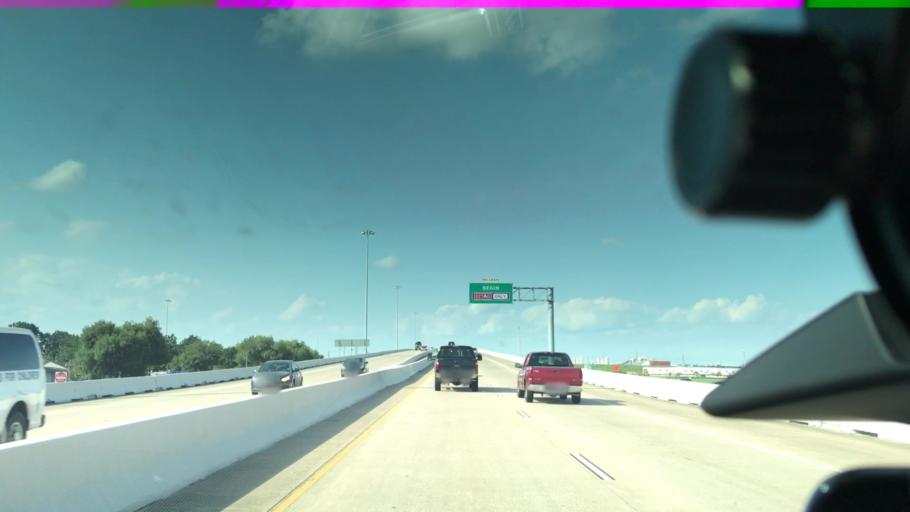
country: US
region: Texas
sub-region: Harris County
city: Deer Park
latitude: 29.7069
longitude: -95.1534
